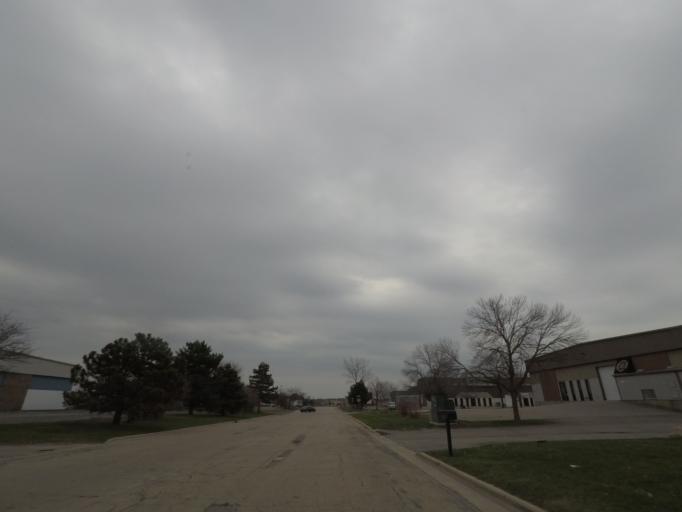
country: US
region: Wisconsin
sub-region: Dane County
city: Middleton
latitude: 43.0984
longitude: -89.5289
